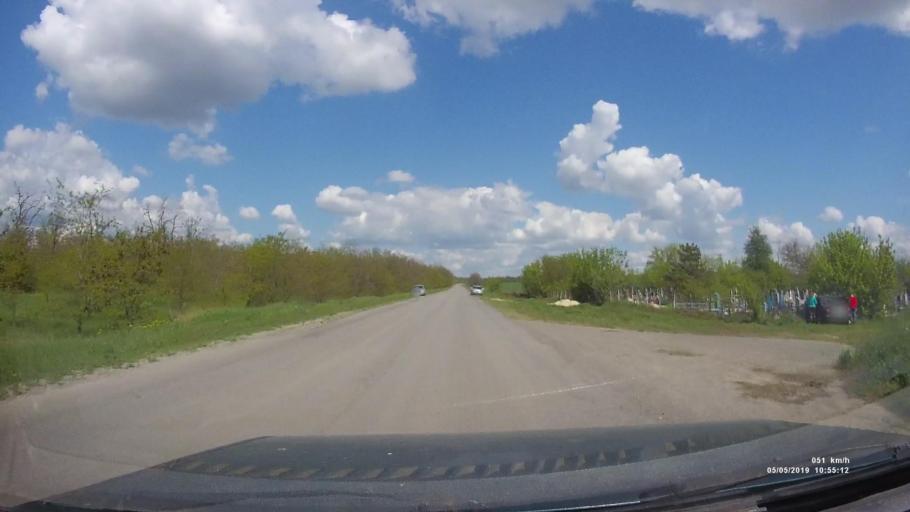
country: RU
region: Rostov
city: Ust'-Donetskiy
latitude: 47.6635
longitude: 40.8216
